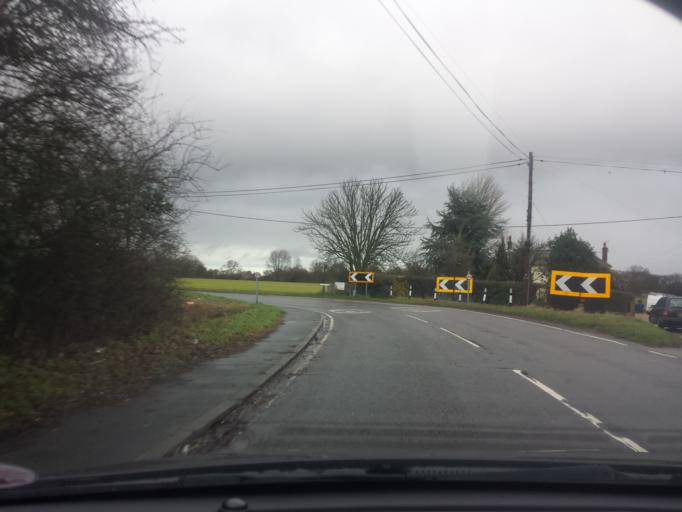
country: GB
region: England
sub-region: Essex
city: Great Bentley
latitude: 51.8815
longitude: 1.1167
